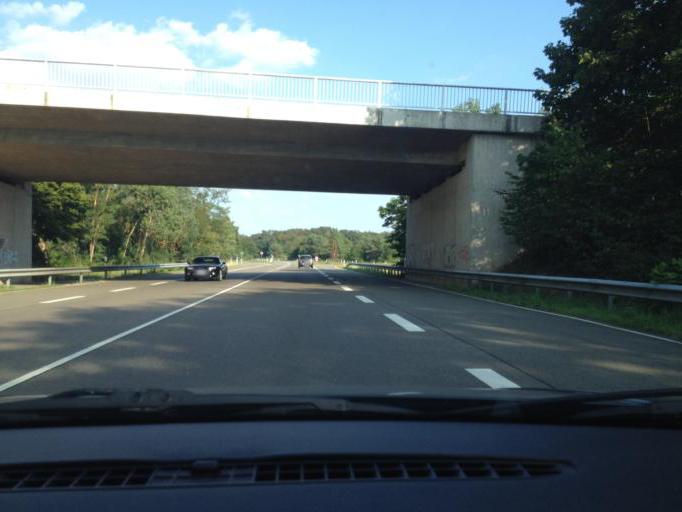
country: DE
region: Rheinland-Pfalz
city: Hanhofen
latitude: 49.3190
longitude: 8.3553
